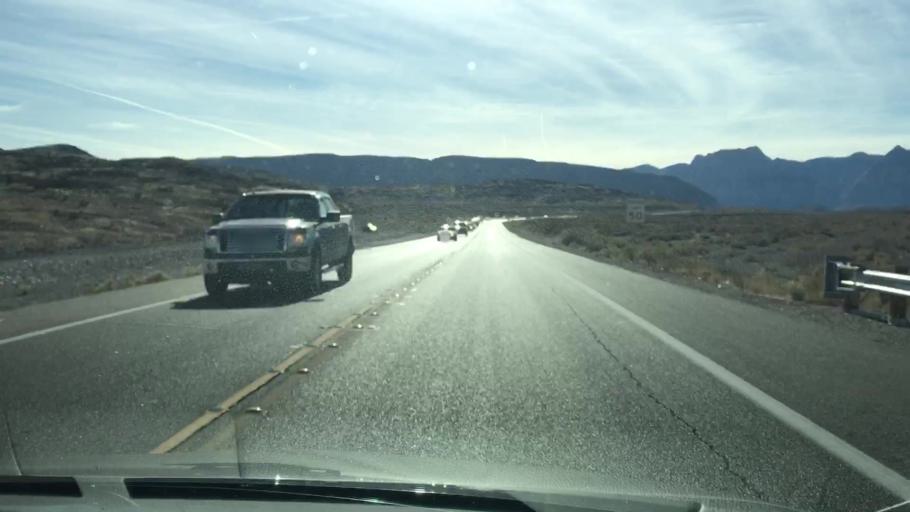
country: US
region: Nevada
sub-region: Clark County
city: Summerlin South
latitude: 36.1564
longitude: -115.3621
